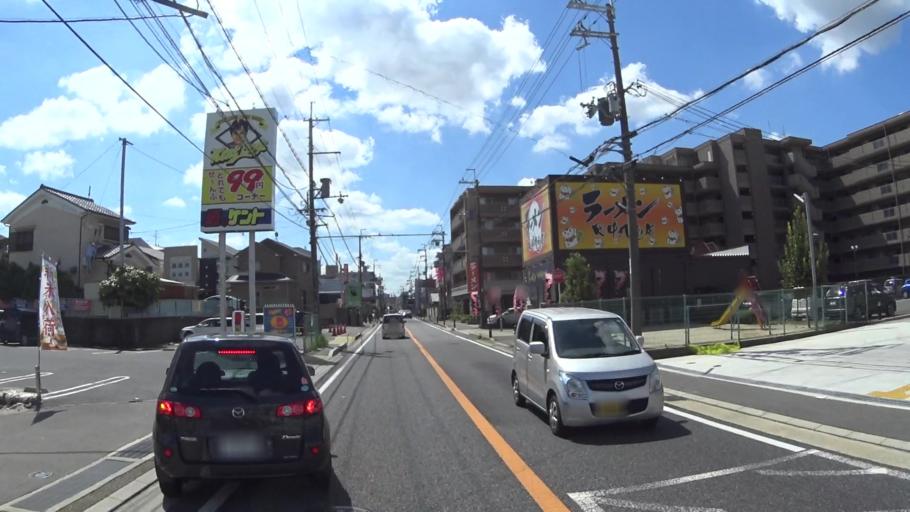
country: JP
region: Kyoto
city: Uji
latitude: 34.8844
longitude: 135.7805
